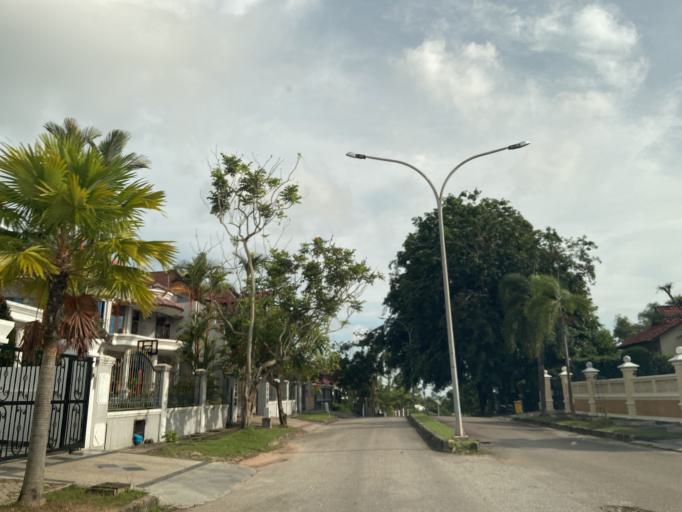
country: SG
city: Singapore
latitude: 1.1087
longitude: 104.0221
